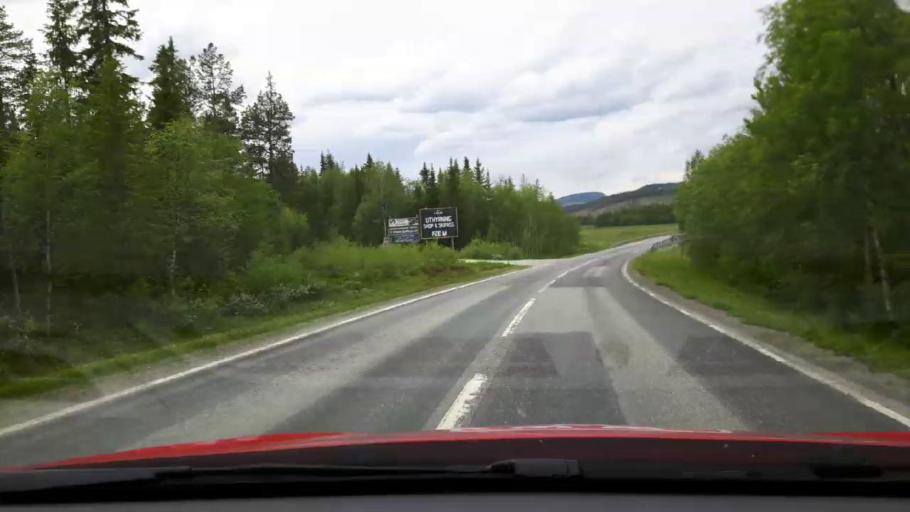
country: NO
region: Hedmark
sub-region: Engerdal
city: Engerdal
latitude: 62.4268
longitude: 12.7220
